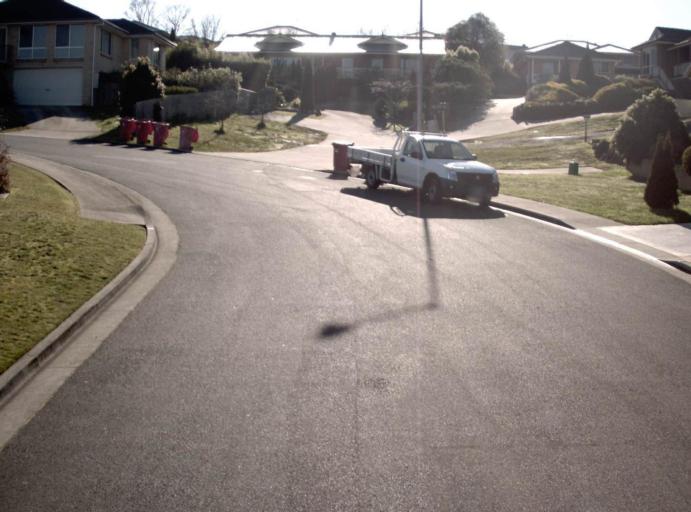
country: AU
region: Tasmania
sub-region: Launceston
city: Summerhill
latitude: -41.4644
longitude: 147.1280
